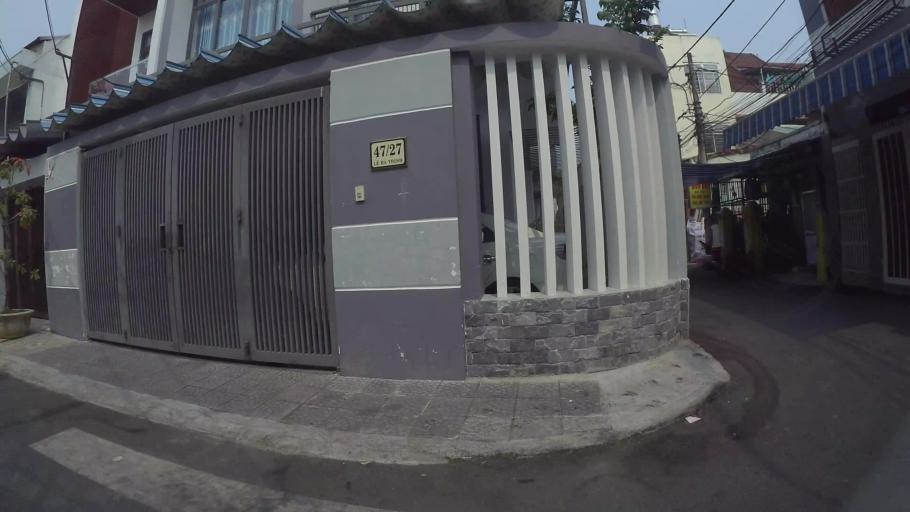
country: VN
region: Da Nang
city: Son Tra
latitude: 16.0430
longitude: 108.2189
